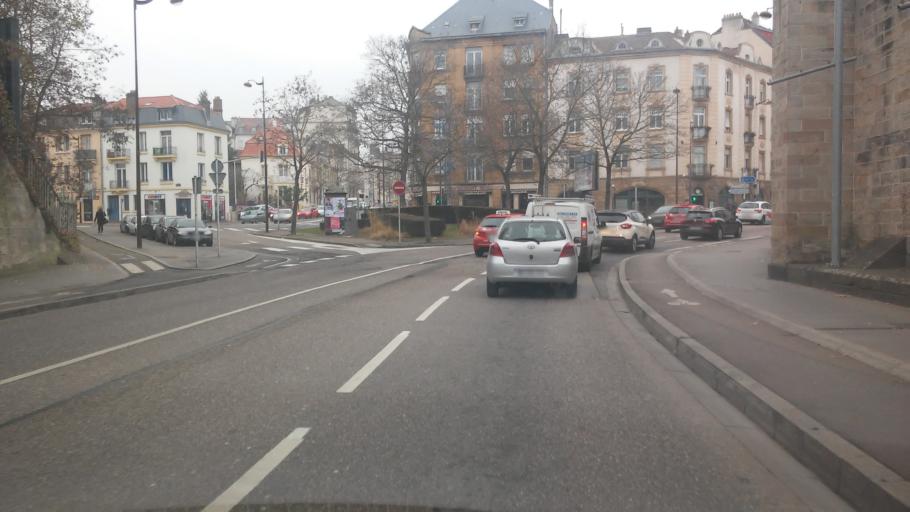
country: FR
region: Lorraine
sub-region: Departement de la Moselle
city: Metz
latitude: 49.1068
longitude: 6.1723
